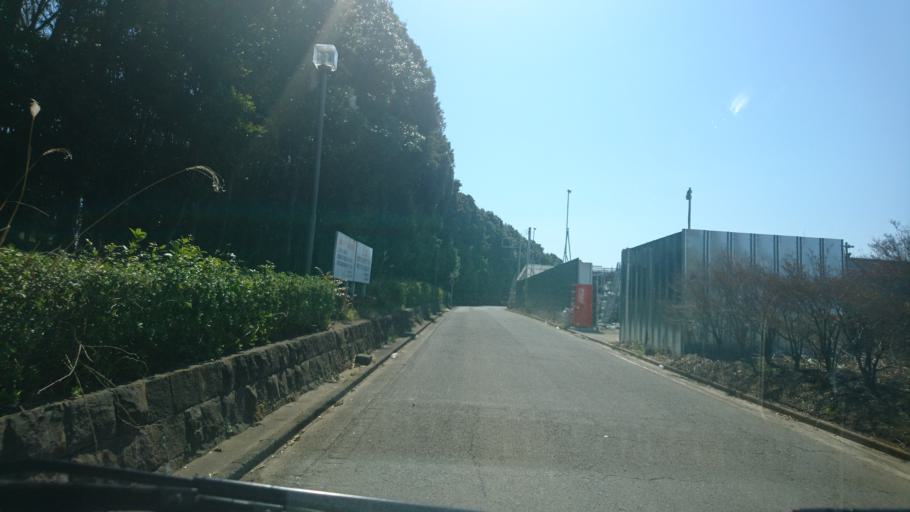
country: JP
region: Kanagawa
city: Fujisawa
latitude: 35.3900
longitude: 139.4249
